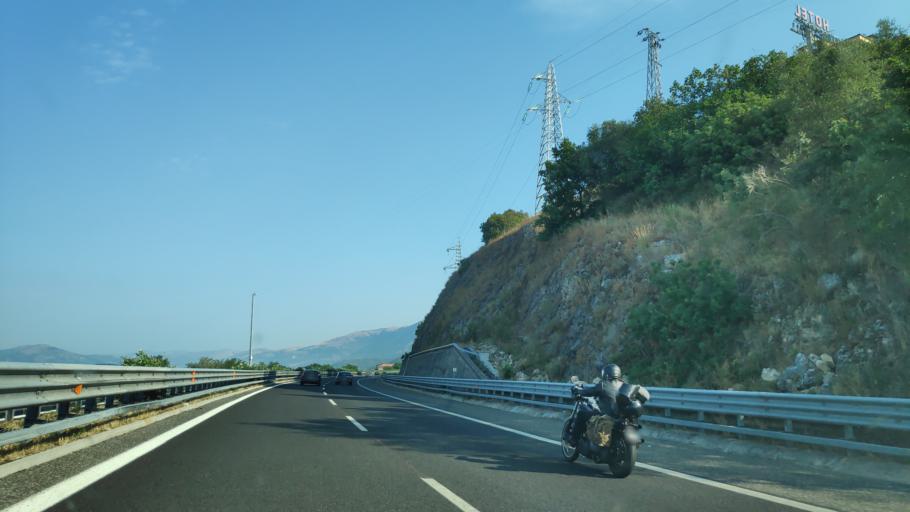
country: IT
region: Campania
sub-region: Provincia di Salerno
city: Atena Lucana
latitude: 40.4515
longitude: 15.5441
